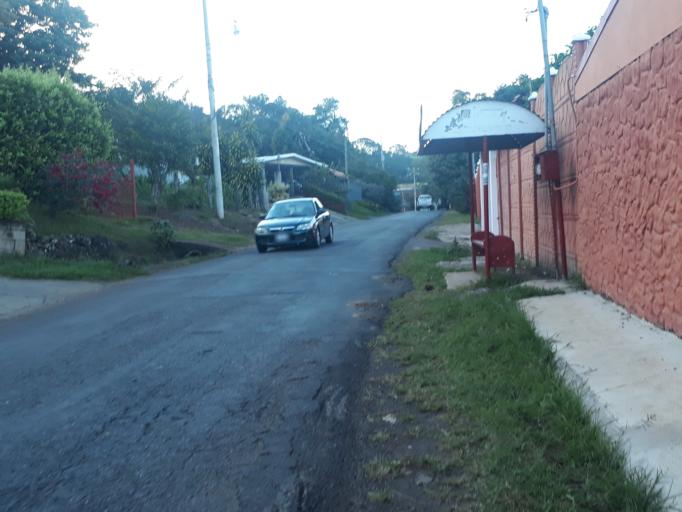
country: CR
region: Alajuela
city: Carrillos
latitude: 10.0396
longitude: -84.3284
